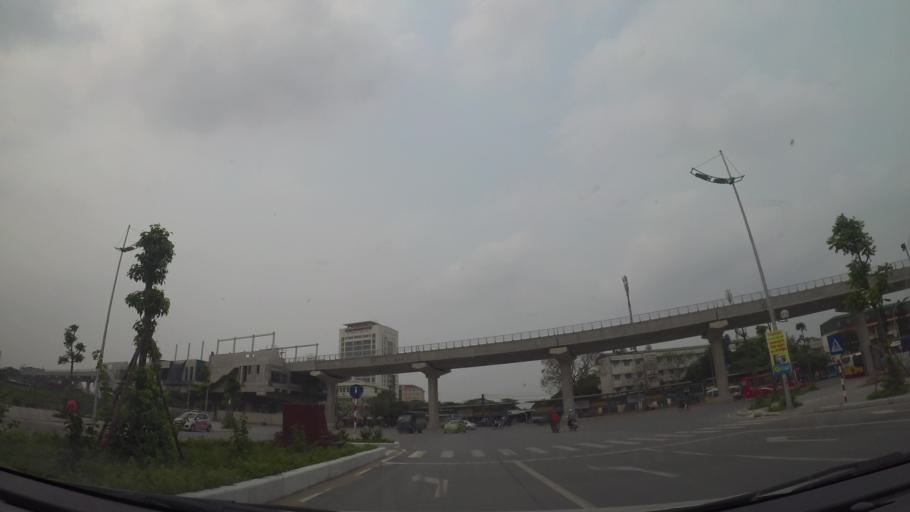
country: VN
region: Ha Noi
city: Cau Dien
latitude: 21.0514
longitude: 105.7358
